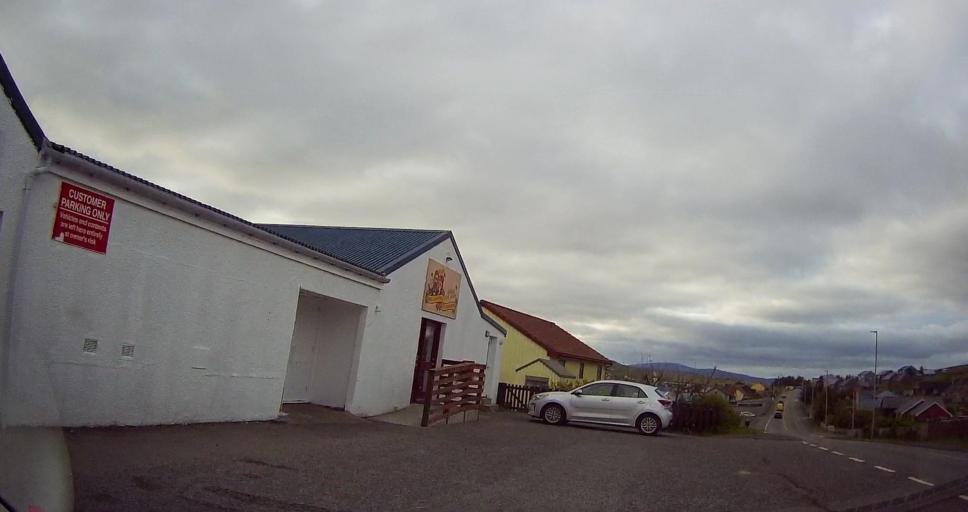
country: GB
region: Scotland
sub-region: Shetland Islands
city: Lerwick
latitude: 60.3890
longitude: -1.3442
